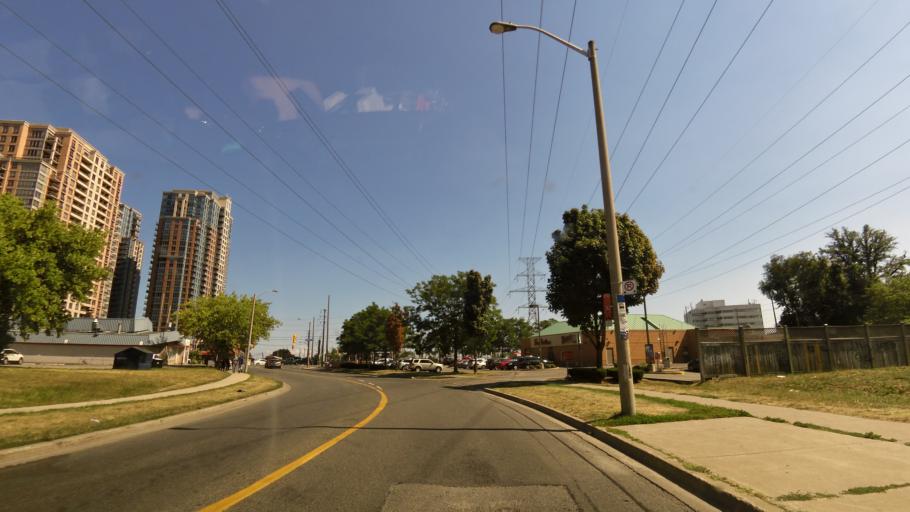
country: CA
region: Ontario
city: Etobicoke
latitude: 43.6391
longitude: -79.5393
